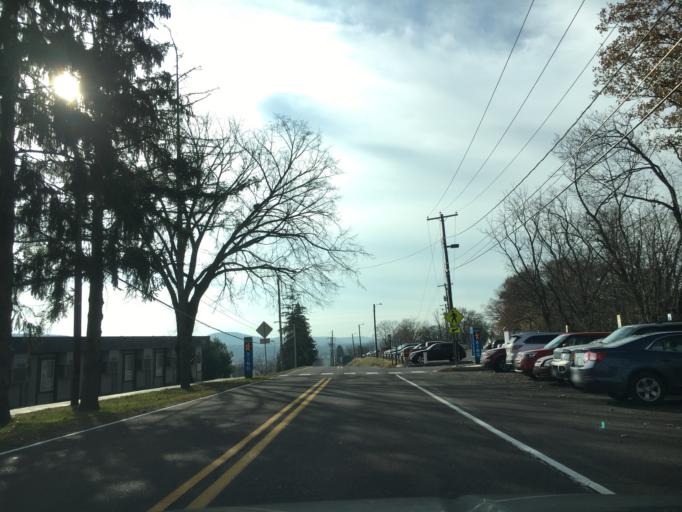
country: US
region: Pennsylvania
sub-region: Montour County
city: Danville
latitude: 40.9688
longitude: -76.6079
